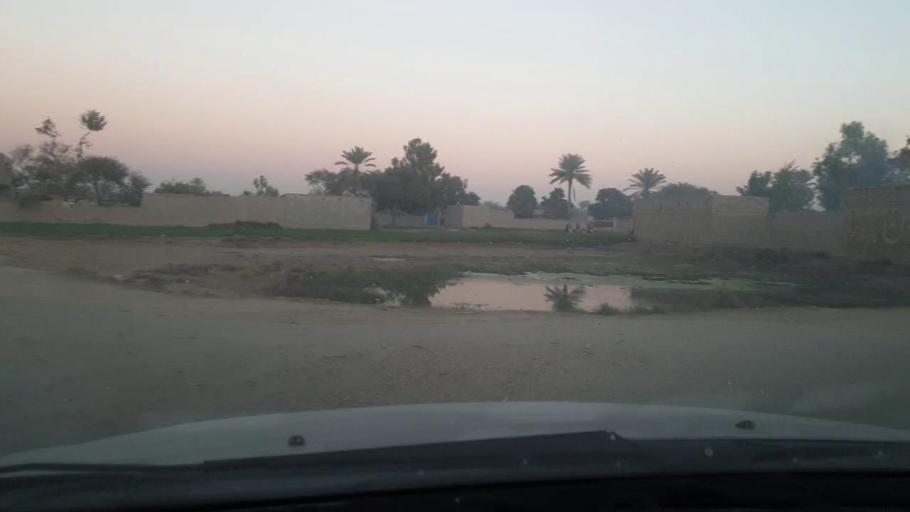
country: PK
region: Sindh
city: Ghotki
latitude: 28.0073
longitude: 69.3377
